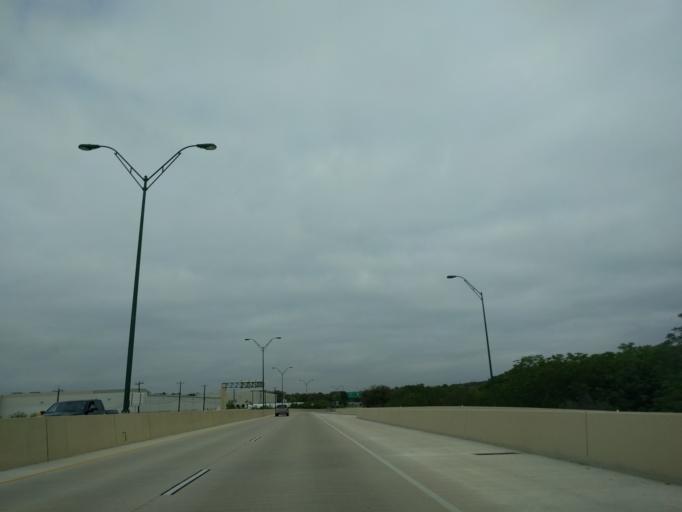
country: US
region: Texas
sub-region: Bexar County
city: Castle Hills
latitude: 29.5498
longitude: -98.4744
